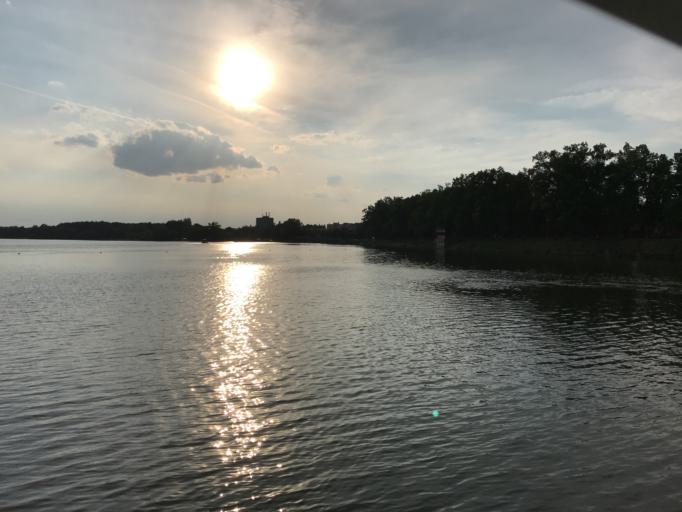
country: CZ
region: Jihocesky
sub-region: Okres Jindrichuv Hradec
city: Trebon
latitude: 49.0003
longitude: 14.7712
